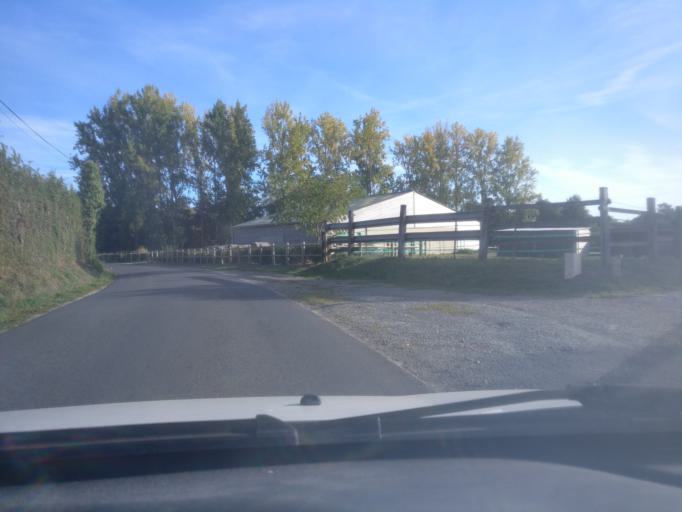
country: FR
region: Lower Normandy
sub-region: Departement de la Manche
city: Sartilly
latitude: 48.7054
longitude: -1.4569
